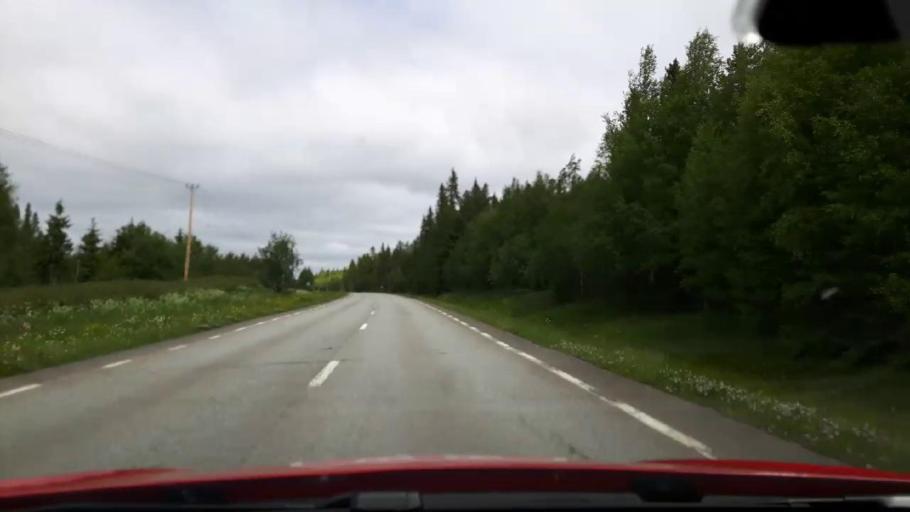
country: SE
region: Jaemtland
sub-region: Krokoms Kommun
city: Krokom
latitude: 63.4766
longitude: 14.5043
